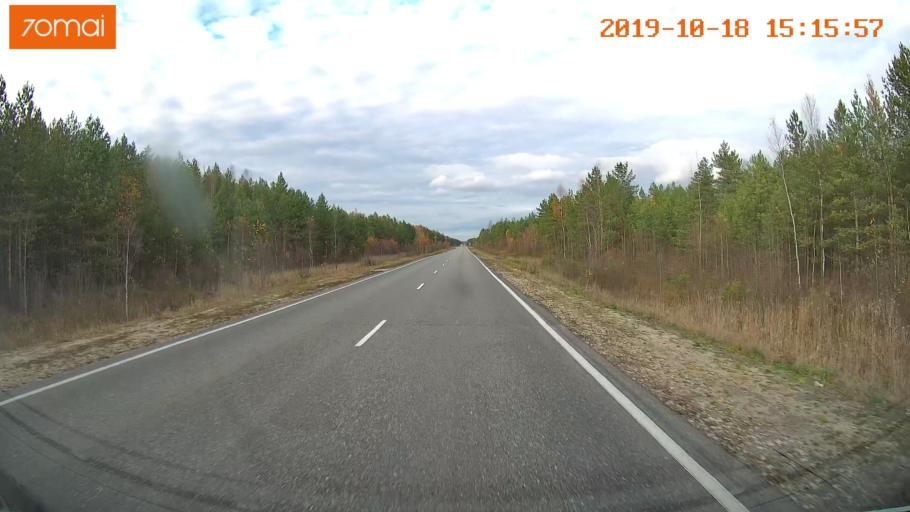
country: RU
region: Vladimir
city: Gus'-Khrustal'nyy
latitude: 55.6278
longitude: 40.7237
